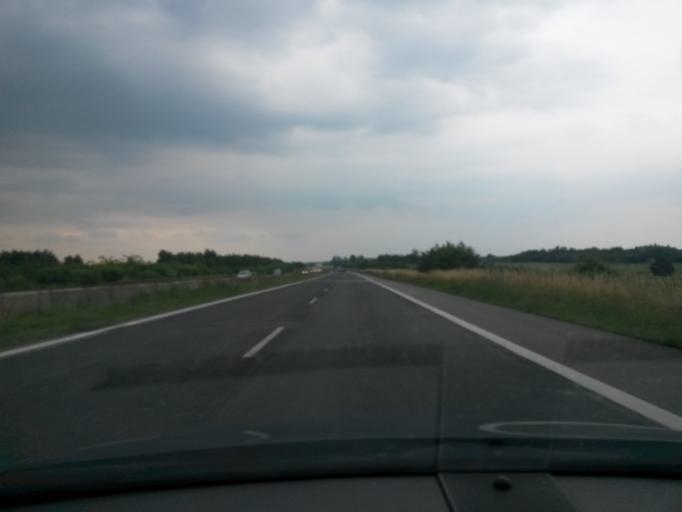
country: PL
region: Silesian Voivodeship
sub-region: Powiat czestochowski
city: Borowno
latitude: 50.9508
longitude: 19.2427
